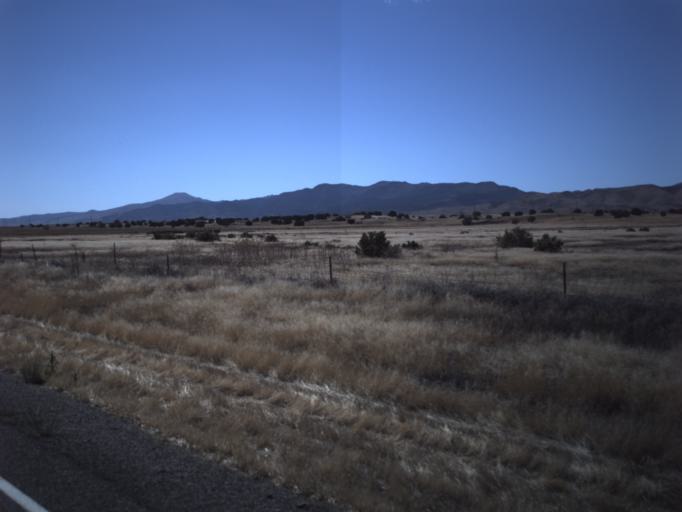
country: US
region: Utah
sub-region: Utah County
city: Genola
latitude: 40.0001
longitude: -111.9578
